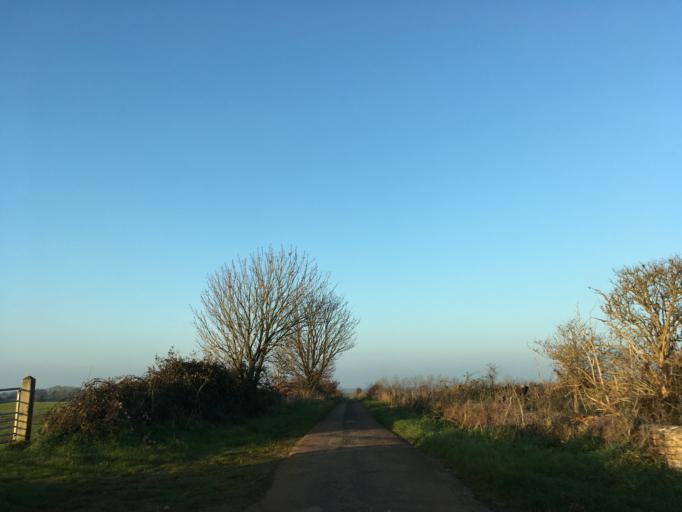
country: GB
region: England
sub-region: Wiltshire
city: Nettleton
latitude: 51.4733
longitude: -2.2820
